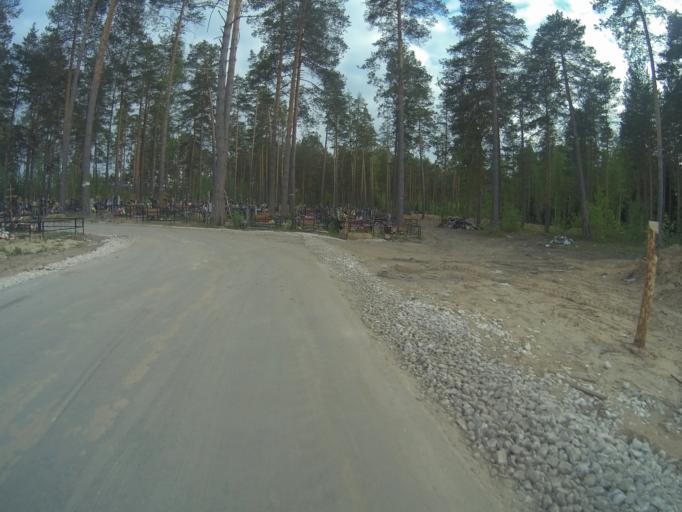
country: RU
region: Vladimir
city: Golovino
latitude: 56.0293
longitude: 40.4176
